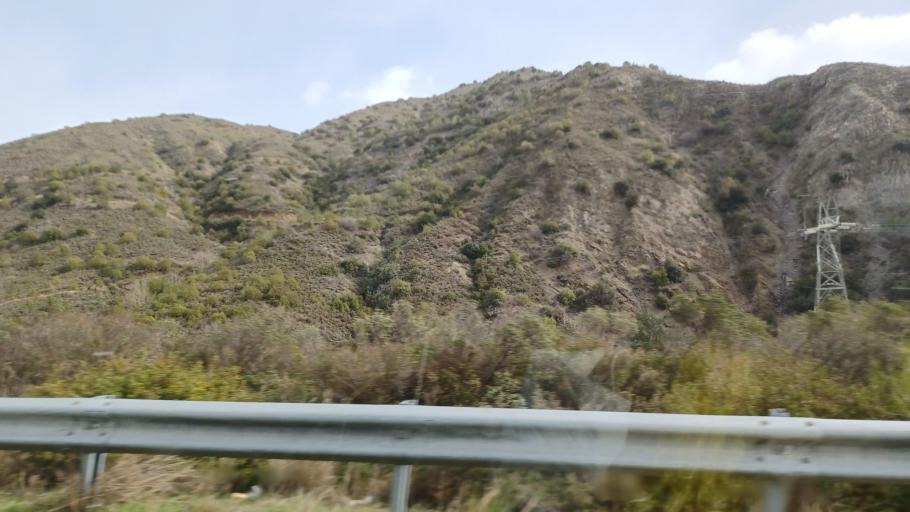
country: CY
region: Limassol
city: Pelendri
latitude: 34.8775
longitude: 32.9222
